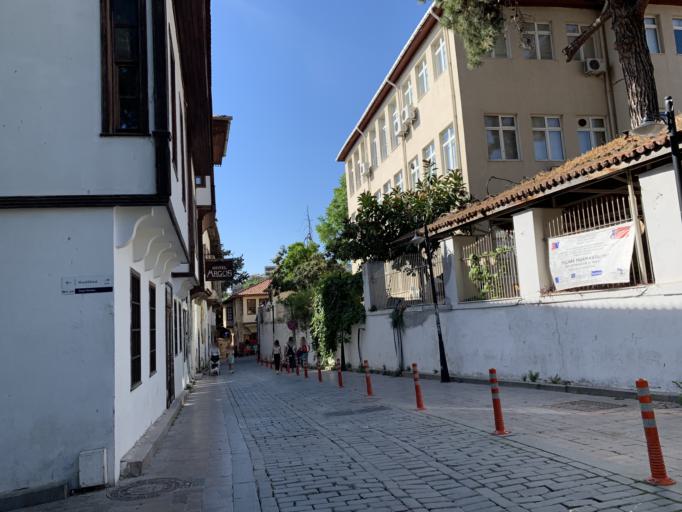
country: TR
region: Antalya
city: Antalya
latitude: 36.8846
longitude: 30.7054
